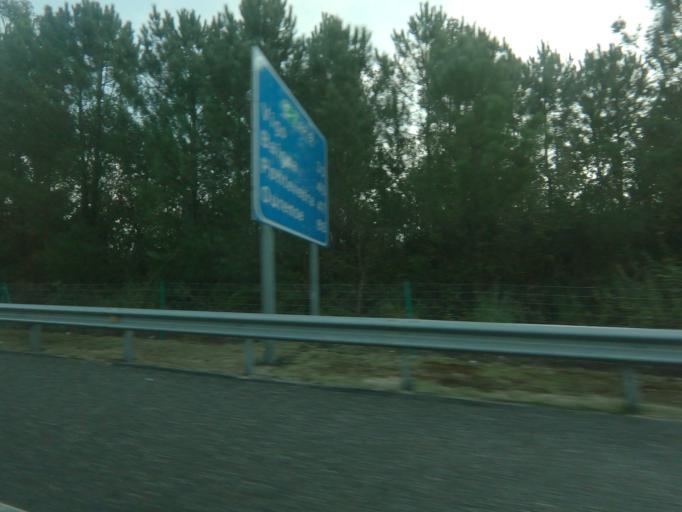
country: ES
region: Galicia
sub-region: Provincia de Pontevedra
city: Tui
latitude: 42.0723
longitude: -8.6394
